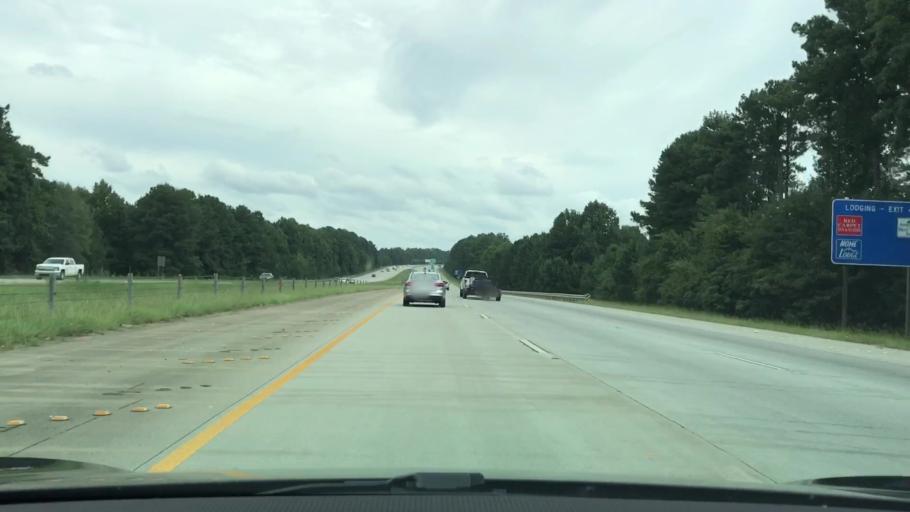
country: US
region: Georgia
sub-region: Coweta County
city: East Newnan
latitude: 33.3028
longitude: -84.7914
